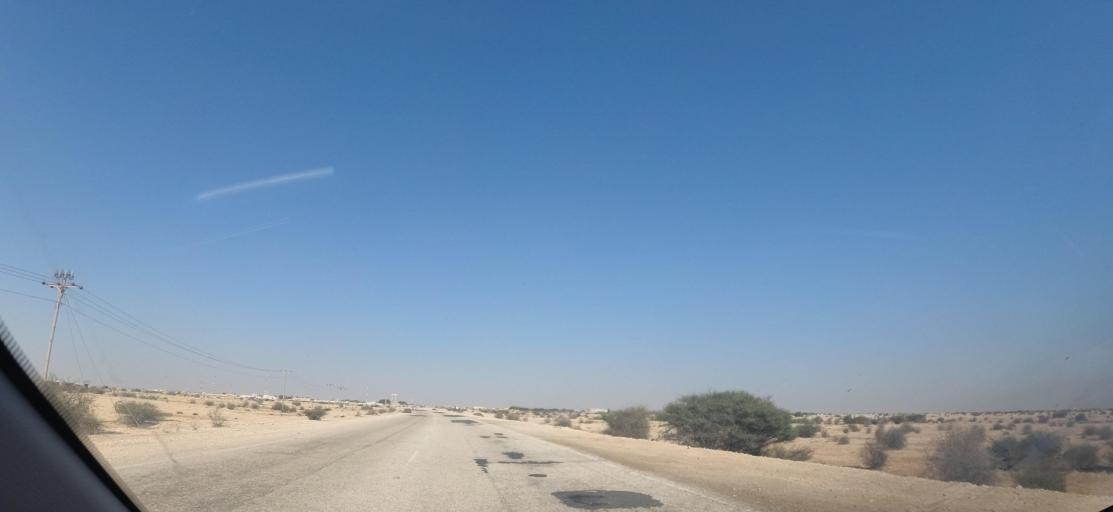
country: QA
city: Al Jumayliyah
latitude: 25.6047
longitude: 51.0750
